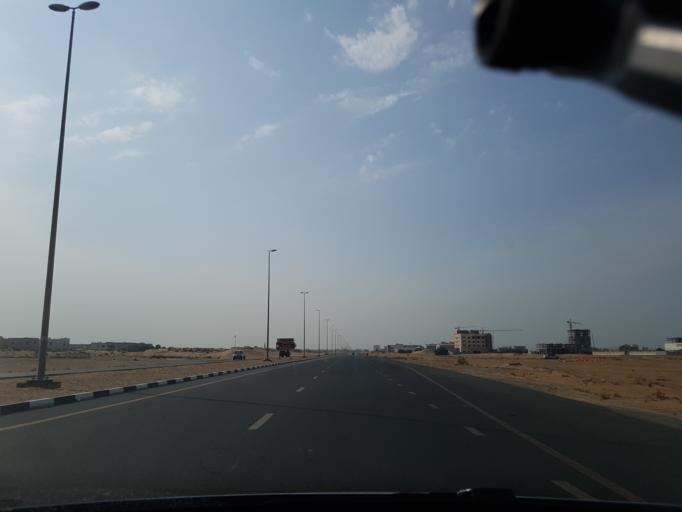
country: AE
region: Ajman
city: Ajman
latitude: 25.4158
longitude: 55.5503
